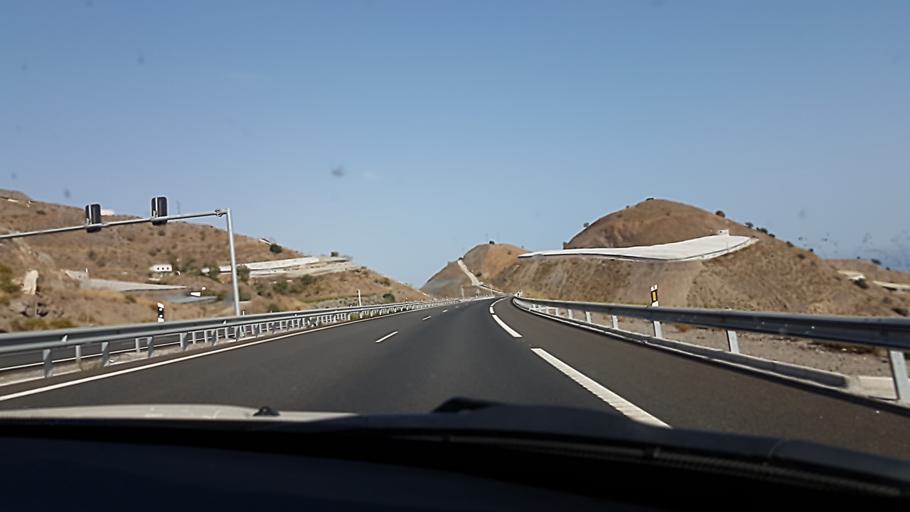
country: ES
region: Andalusia
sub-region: Provincia de Granada
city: Polopos
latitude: 36.7520
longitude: -3.2897
